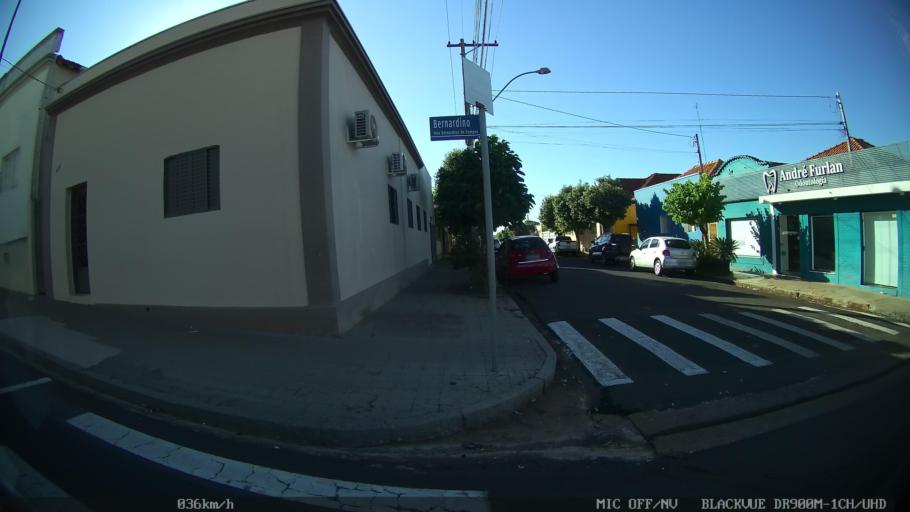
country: BR
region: Sao Paulo
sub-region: Olimpia
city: Olimpia
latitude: -20.7373
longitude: -48.9126
